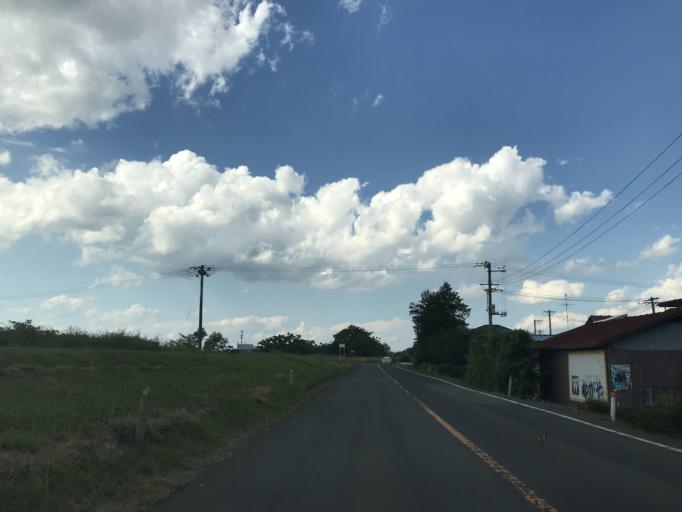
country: JP
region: Miyagi
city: Wakuya
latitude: 38.6753
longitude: 141.2074
